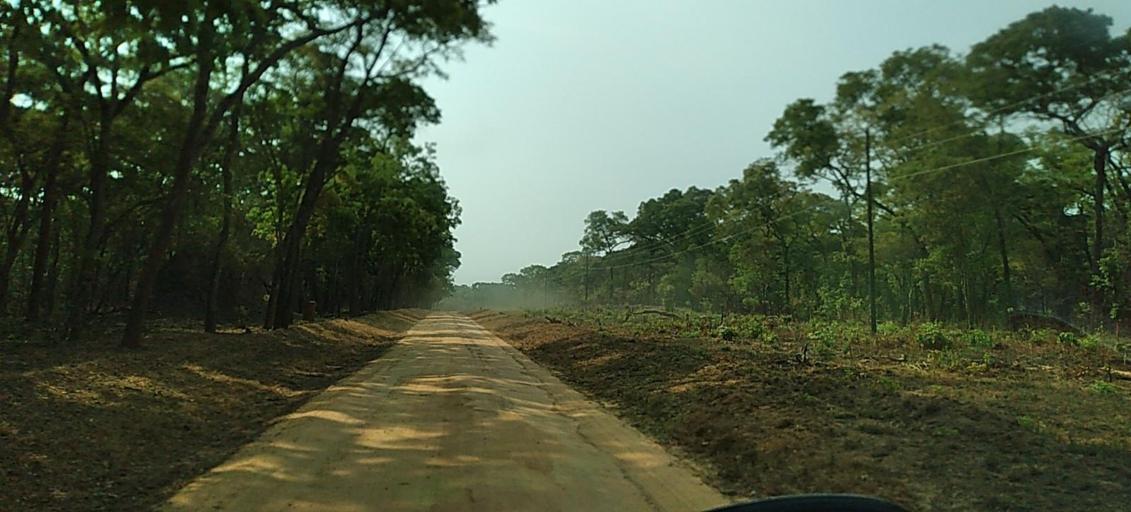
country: ZM
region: North-Western
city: Solwezi
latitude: -12.6889
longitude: 26.3983
